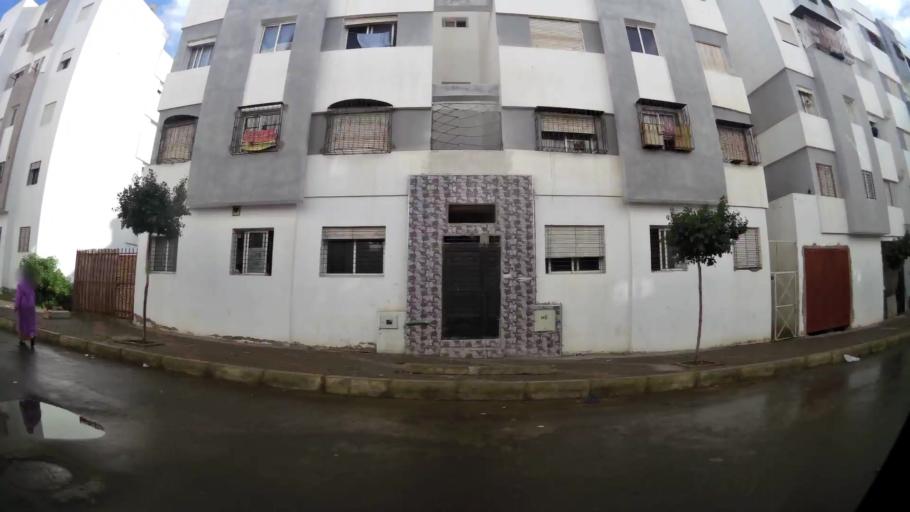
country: MA
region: Grand Casablanca
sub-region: Casablanca
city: Casablanca
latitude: 33.5566
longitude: -7.7003
